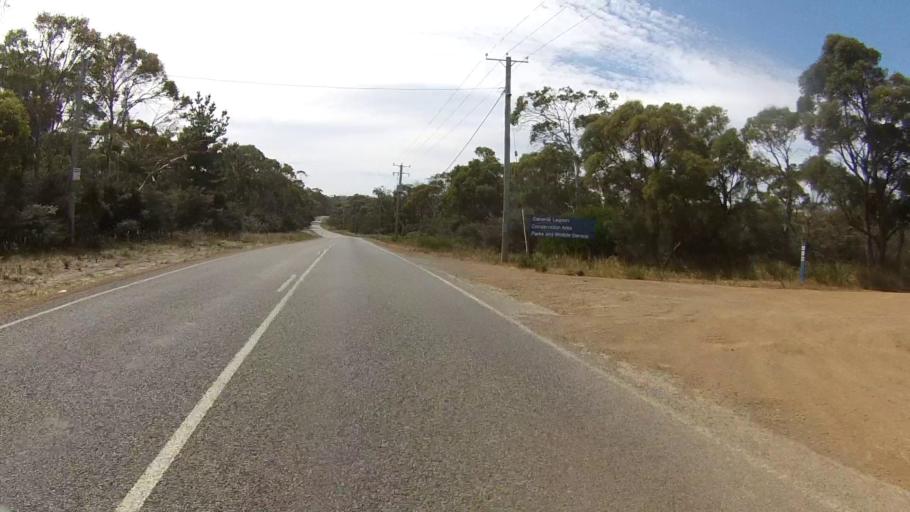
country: AU
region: Tasmania
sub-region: Clarence
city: Sandford
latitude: -43.0213
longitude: 147.4878
